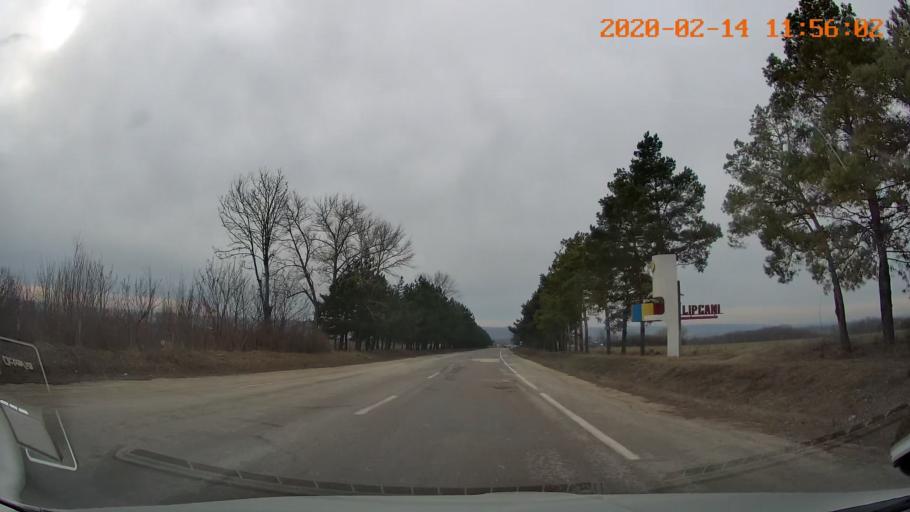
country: RO
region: Botosani
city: Radauti
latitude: 48.2734
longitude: 26.8273
